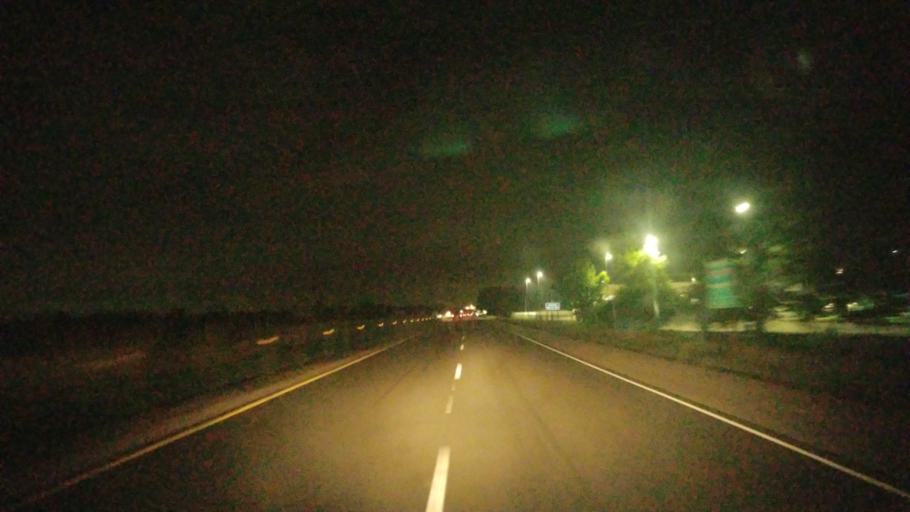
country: US
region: Illinois
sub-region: Madison County
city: Mitchell
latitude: 38.7578
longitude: -90.0740
